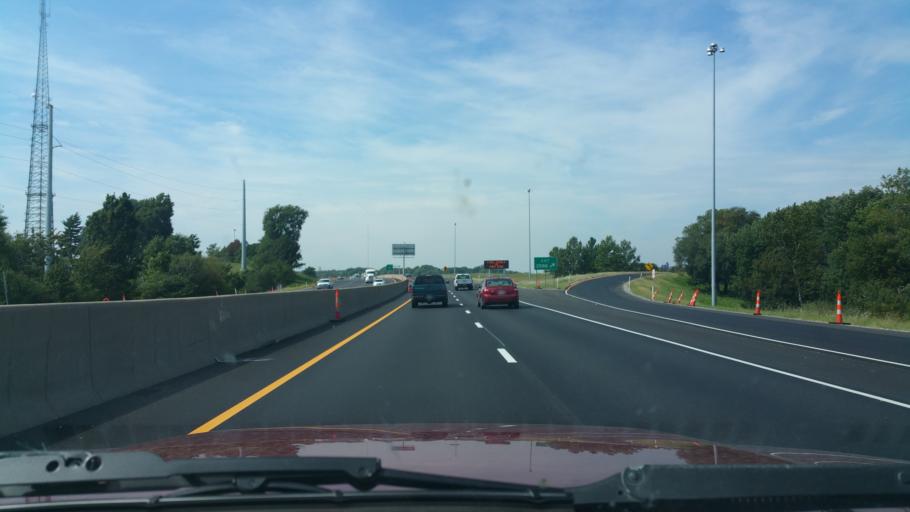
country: US
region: Kansas
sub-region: Shawnee County
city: Topeka
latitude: 39.0681
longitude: -95.7190
